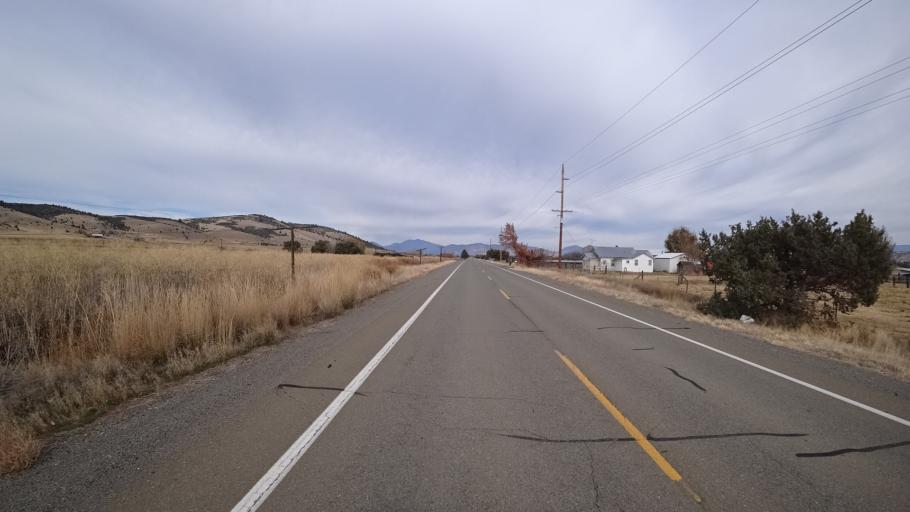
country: US
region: California
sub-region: Siskiyou County
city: Montague
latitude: 41.6610
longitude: -122.5208
